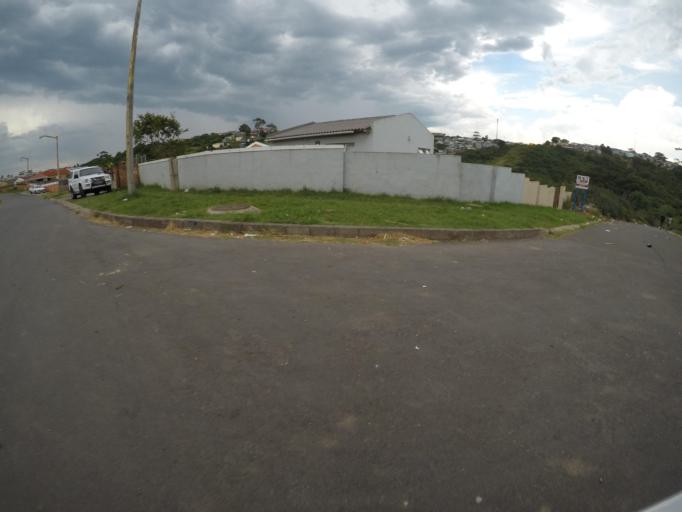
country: ZA
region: Eastern Cape
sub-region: Buffalo City Metropolitan Municipality
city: East London
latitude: -33.0192
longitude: 27.8686
